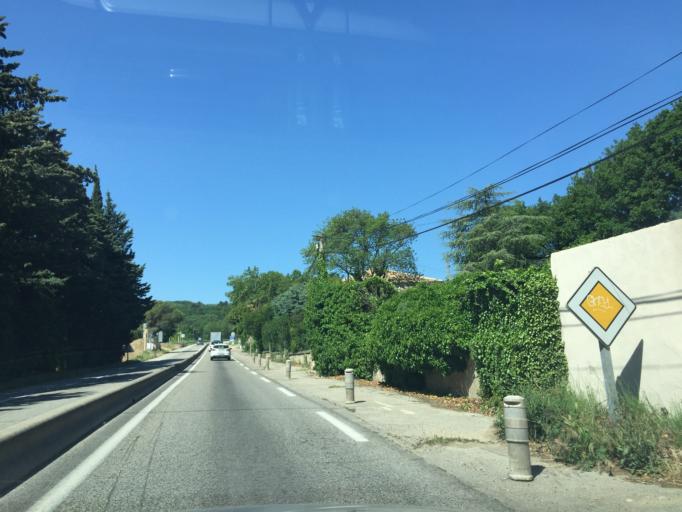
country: FR
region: Languedoc-Roussillon
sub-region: Departement du Gard
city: Saze
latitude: 43.9468
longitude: 4.6827
